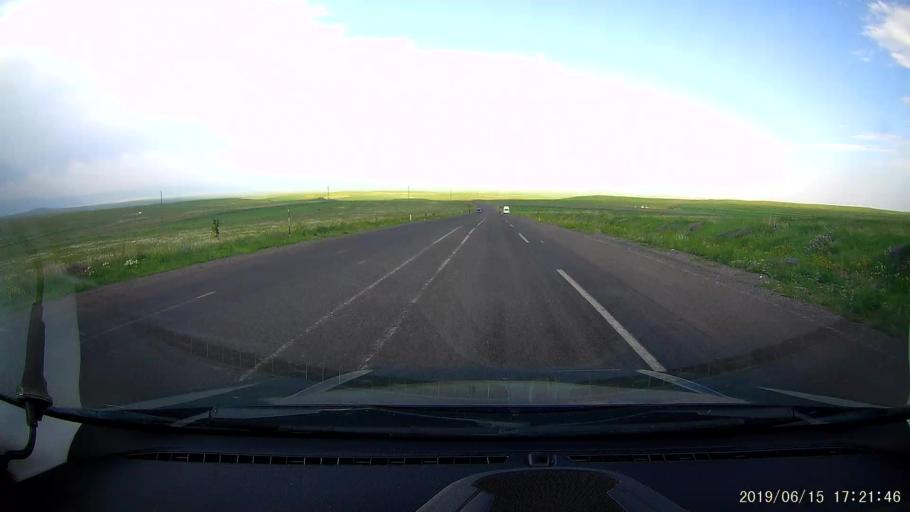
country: TR
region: Kars
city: Basgedikler
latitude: 40.6171
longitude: 43.3309
